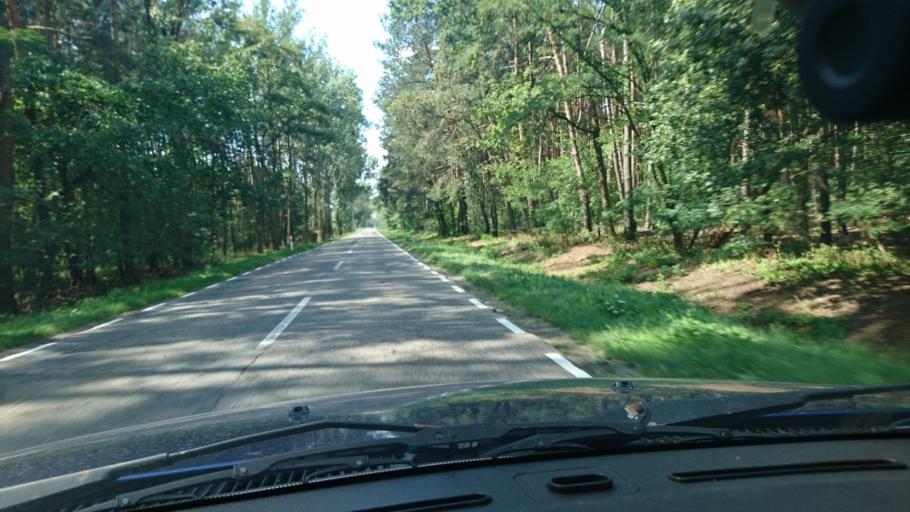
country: PL
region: Greater Poland Voivodeship
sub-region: Powiat ostrowski
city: Odolanow
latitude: 51.5920
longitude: 17.6315
